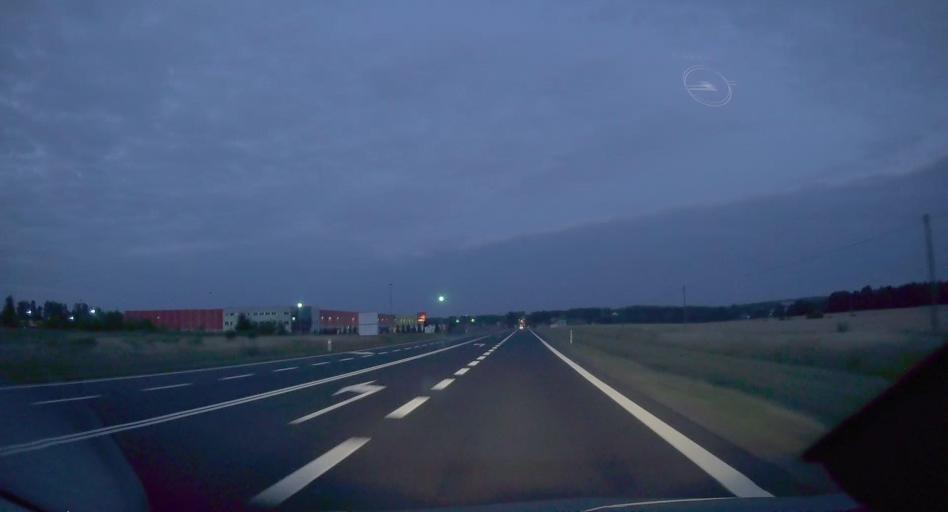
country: PL
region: Silesian Voivodeship
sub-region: Powiat klobucki
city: Klobuck
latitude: 50.8876
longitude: 18.9750
